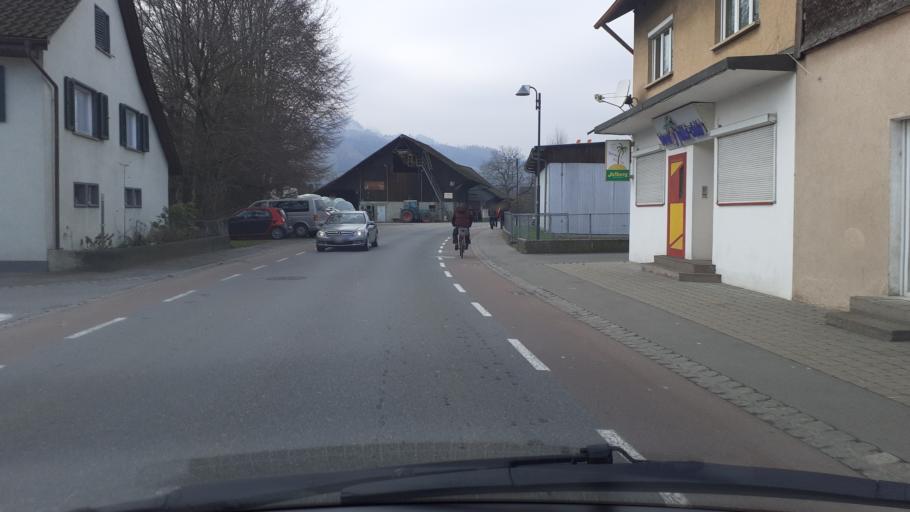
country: AT
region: Vorarlberg
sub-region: Politischer Bezirk Bregenz
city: Hochst
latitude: 47.4595
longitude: 9.6364
